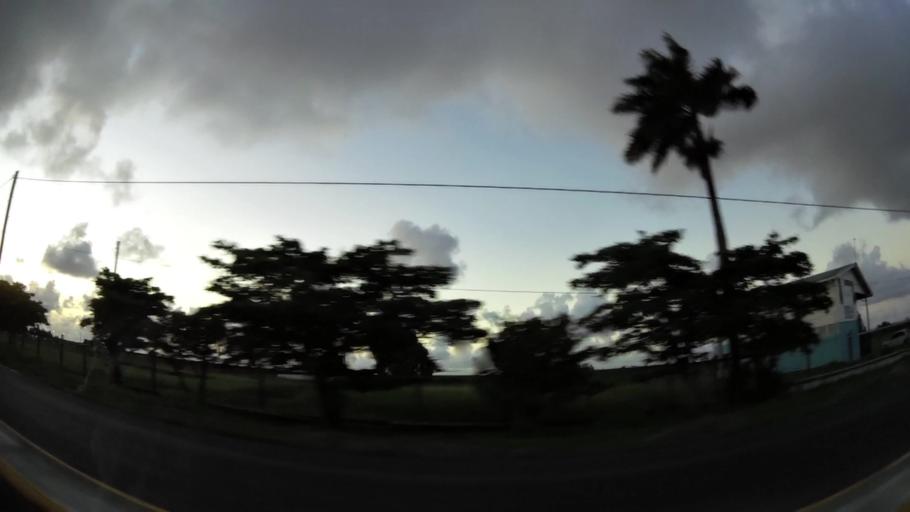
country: GY
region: Demerara-Mahaica
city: Georgetown
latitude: 6.8237
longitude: -58.1500
